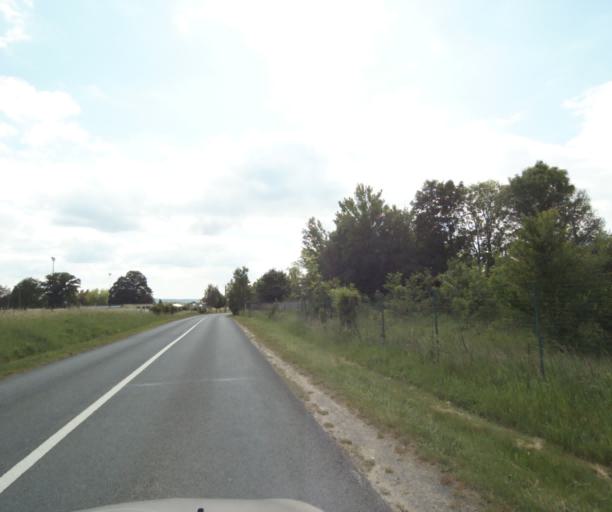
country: FR
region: Champagne-Ardenne
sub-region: Departement des Ardennes
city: Saint-Laurent
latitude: 49.7674
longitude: 4.7776
